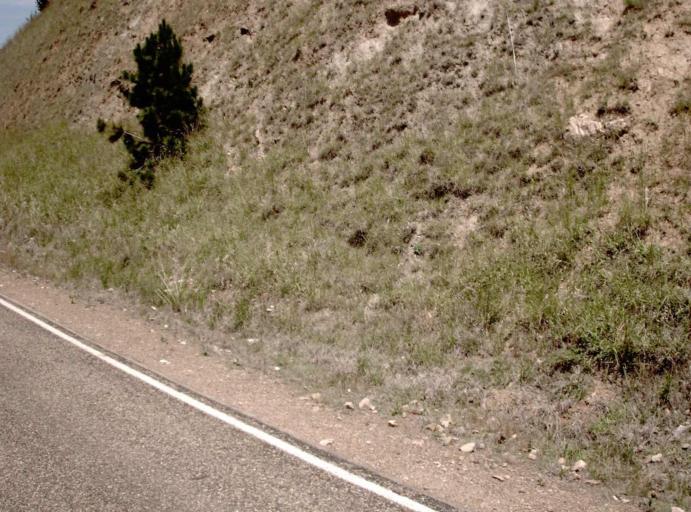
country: AU
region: Victoria
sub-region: East Gippsland
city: Bairnsdale
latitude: -37.3835
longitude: 147.8306
